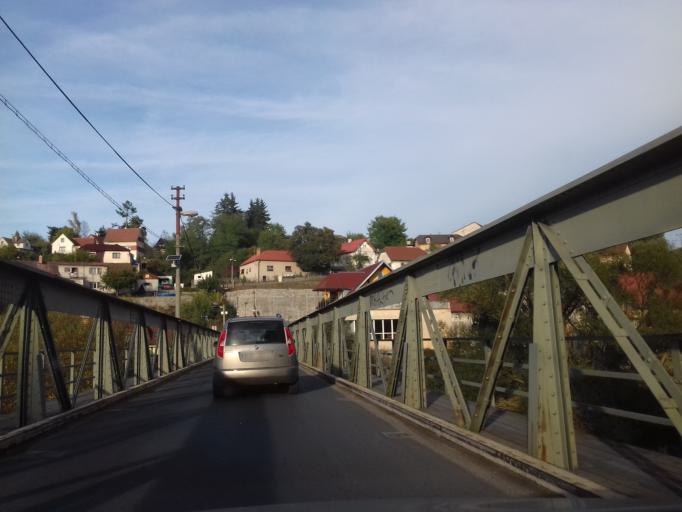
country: CZ
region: Central Bohemia
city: Kamenny Privoz
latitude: 49.8610
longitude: 14.5041
